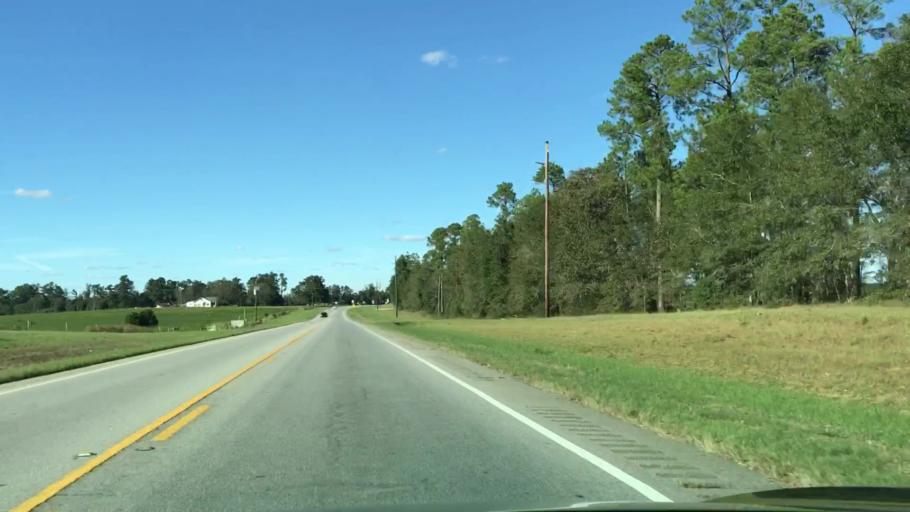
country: US
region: Georgia
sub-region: Jefferson County
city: Louisville
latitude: 33.0633
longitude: -82.4062
